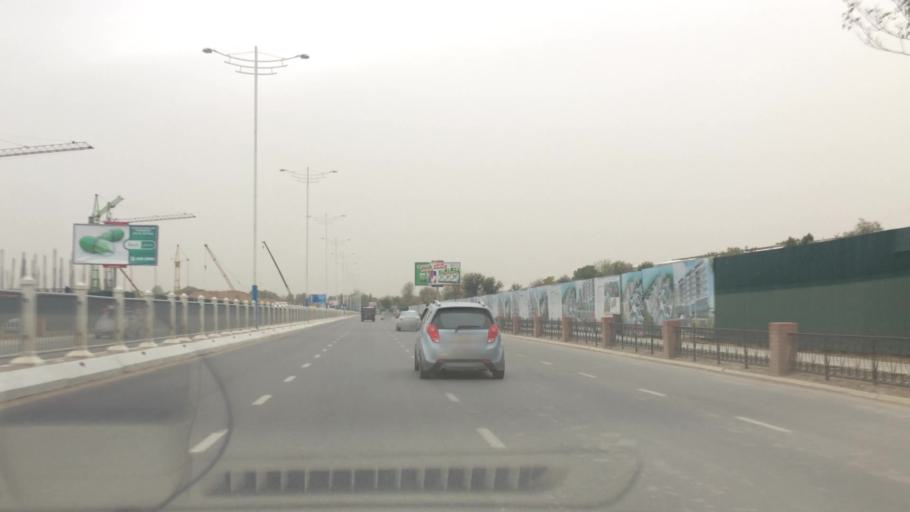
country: UZ
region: Toshkent
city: Salor
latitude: 41.3052
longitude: 69.3293
